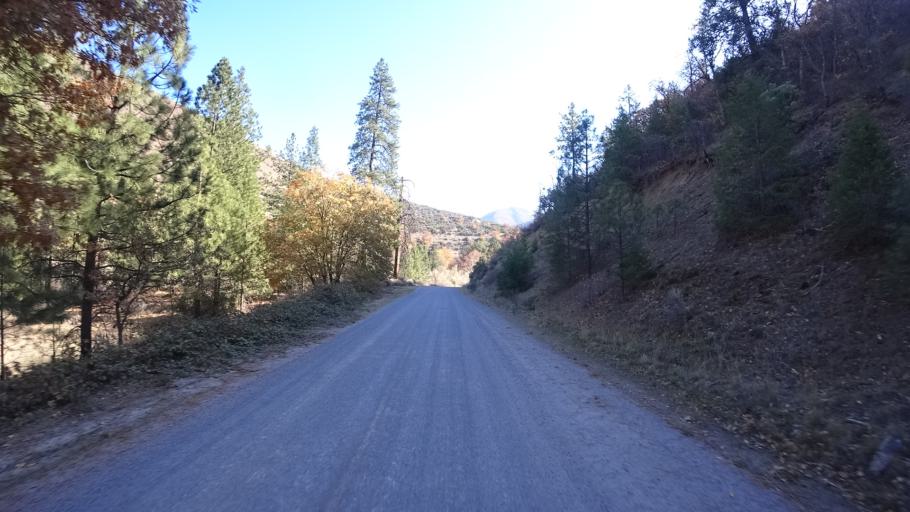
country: US
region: California
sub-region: Siskiyou County
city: Yreka
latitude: 41.8326
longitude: -122.6637
